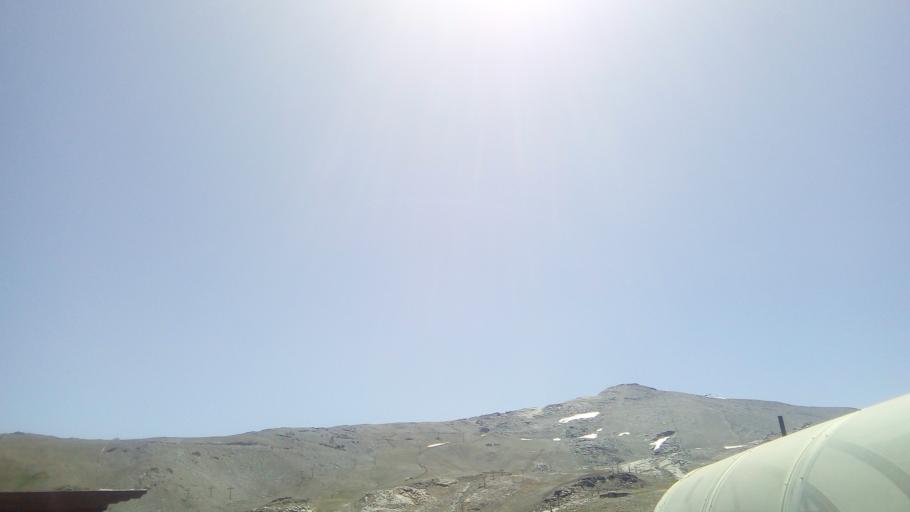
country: ES
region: Andalusia
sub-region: Provincia de Granada
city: Guejar-Sierra
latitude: 37.0710
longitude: -3.3908
